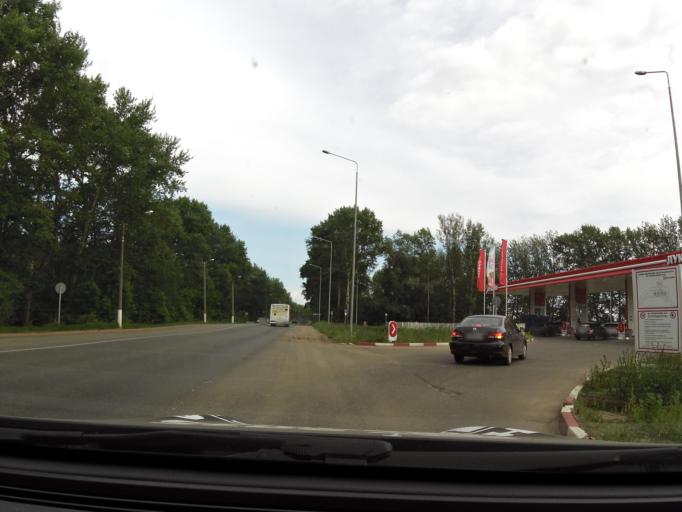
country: RU
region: Kirov
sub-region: Kirovo-Chepetskiy Rayon
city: Kirov
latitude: 58.6187
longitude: 49.7141
